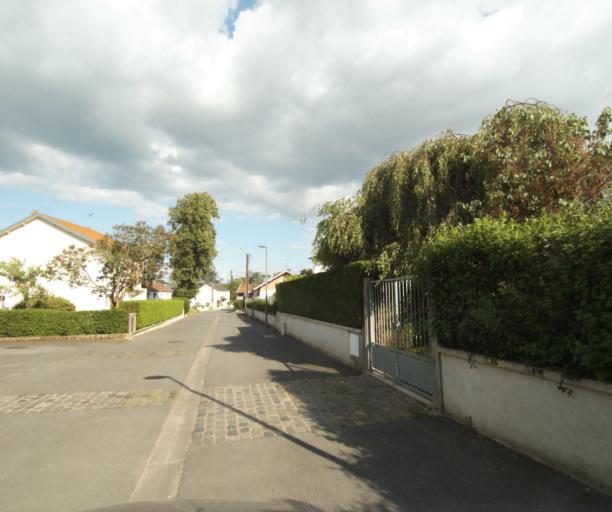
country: FR
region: Champagne-Ardenne
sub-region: Departement des Ardennes
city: Montcy-Notre-Dame
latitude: 49.7814
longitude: 4.7276
